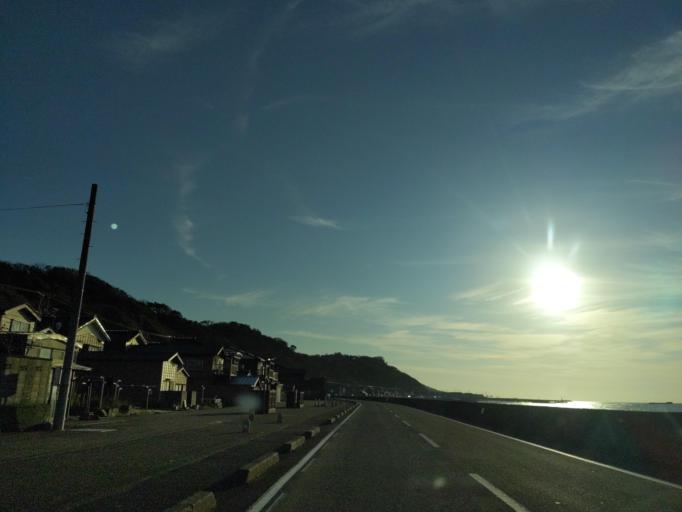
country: JP
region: Niigata
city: Nagaoka
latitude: 37.5494
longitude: 138.6975
